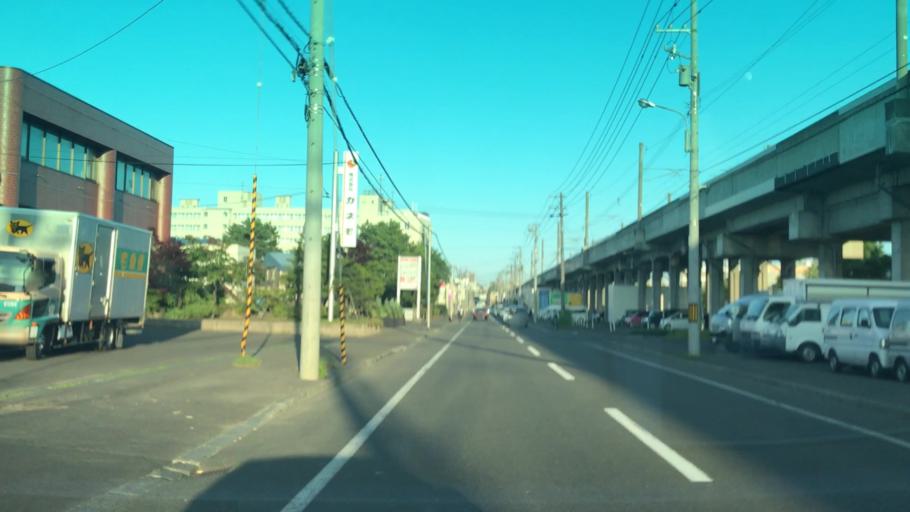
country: JP
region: Hokkaido
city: Sapporo
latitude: 43.0788
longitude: 141.3135
